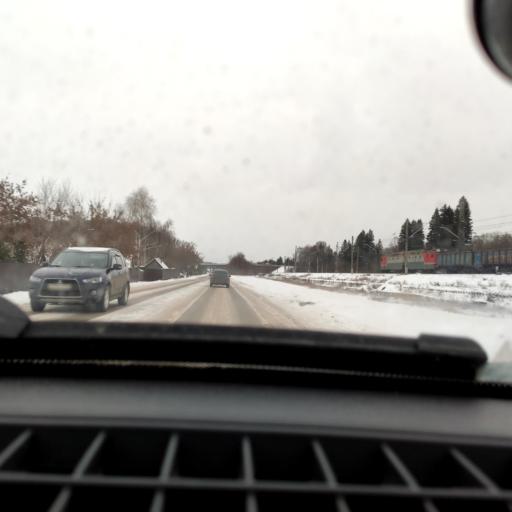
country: RU
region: Bashkortostan
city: Iglino
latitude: 54.8305
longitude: 56.4161
